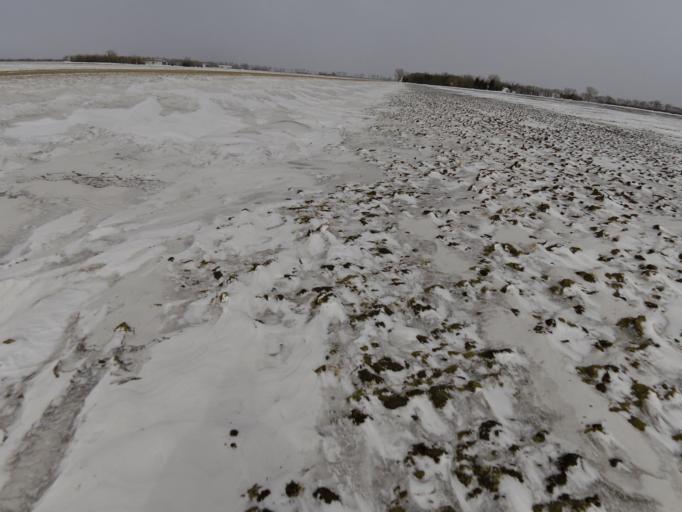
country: US
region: North Dakota
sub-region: Walsh County
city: Grafton
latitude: 48.3990
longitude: -97.2118
